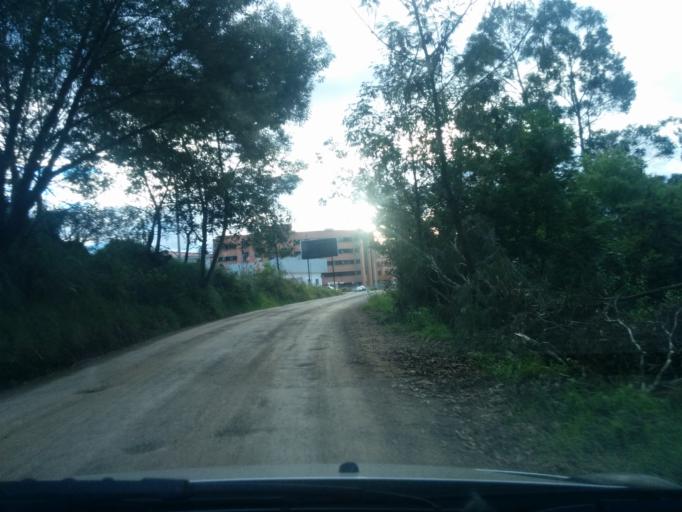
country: EC
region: Azuay
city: Cuenca
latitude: -2.8919
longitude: -78.9589
